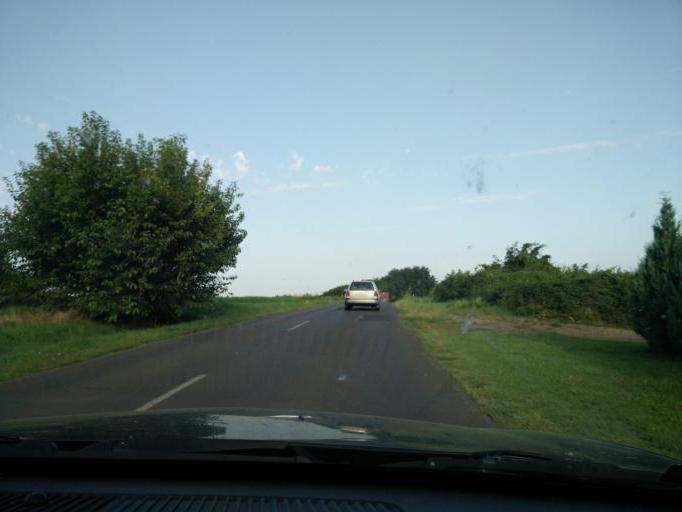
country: HU
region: Tolna
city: Nagymanyok
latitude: 46.2791
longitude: 18.4498
